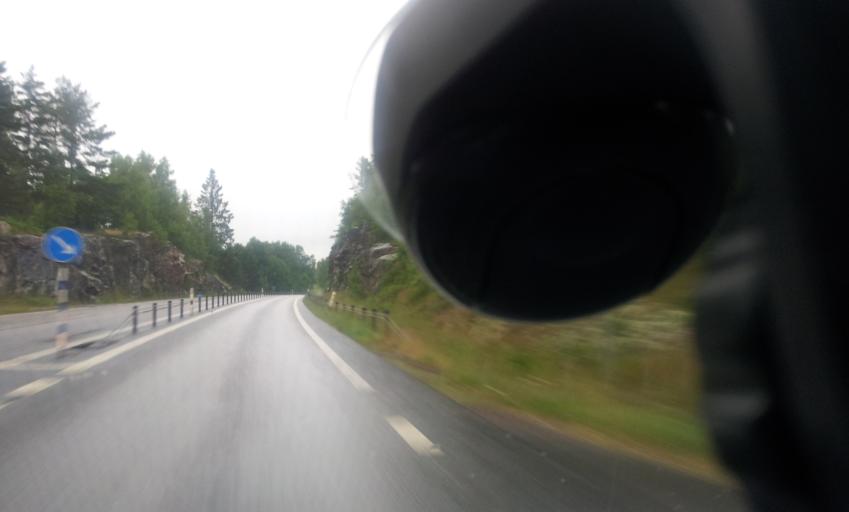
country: SE
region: Kalmar
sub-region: Vasterviks Kommun
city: Forserum
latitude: 57.9823
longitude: 16.4827
